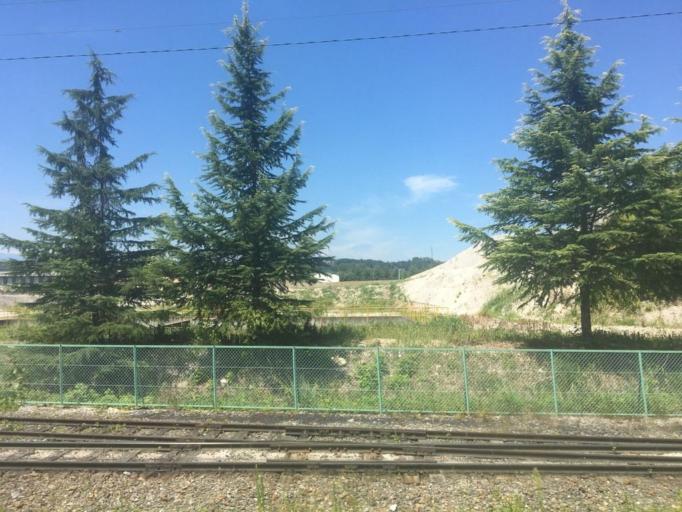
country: JP
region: Saitama
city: Chichibu
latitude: 36.0323
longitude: 139.0973
